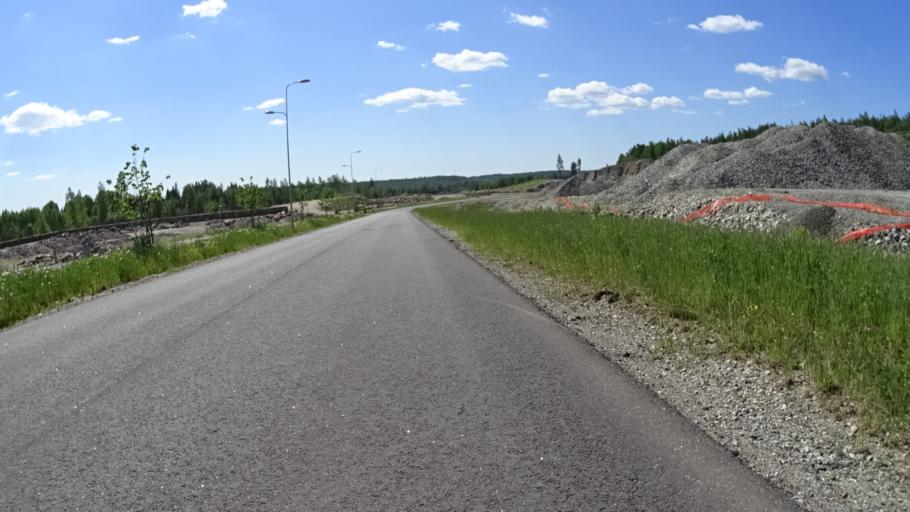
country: FI
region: Uusimaa
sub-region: Helsinki
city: Nurmijaervi
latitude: 60.4425
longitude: 24.8349
